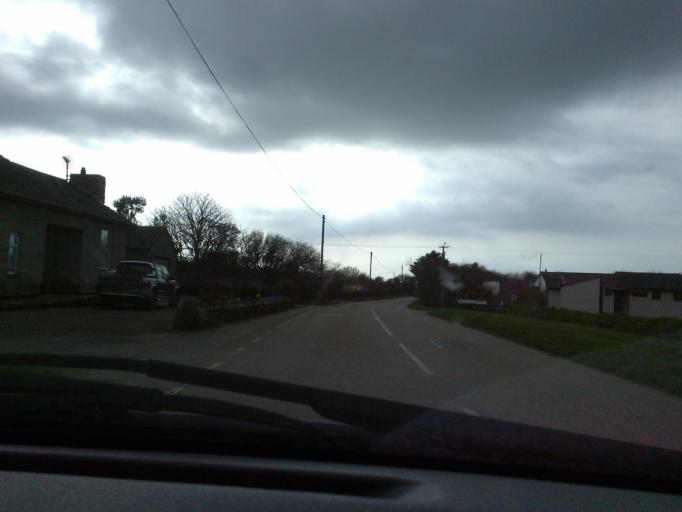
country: GB
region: England
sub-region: Cornwall
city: Sennen
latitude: 50.0562
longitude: -5.6639
